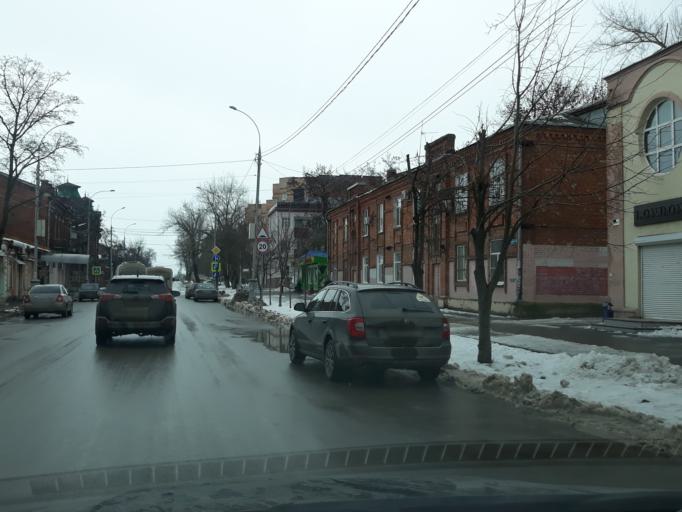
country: RU
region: Rostov
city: Taganrog
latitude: 47.2089
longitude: 38.9393
